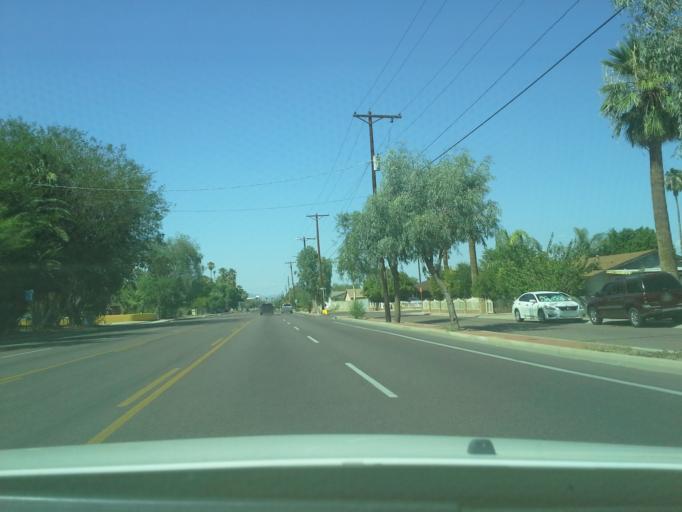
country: US
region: Arizona
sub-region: Maricopa County
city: Phoenix
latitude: 33.3815
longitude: -112.0646
